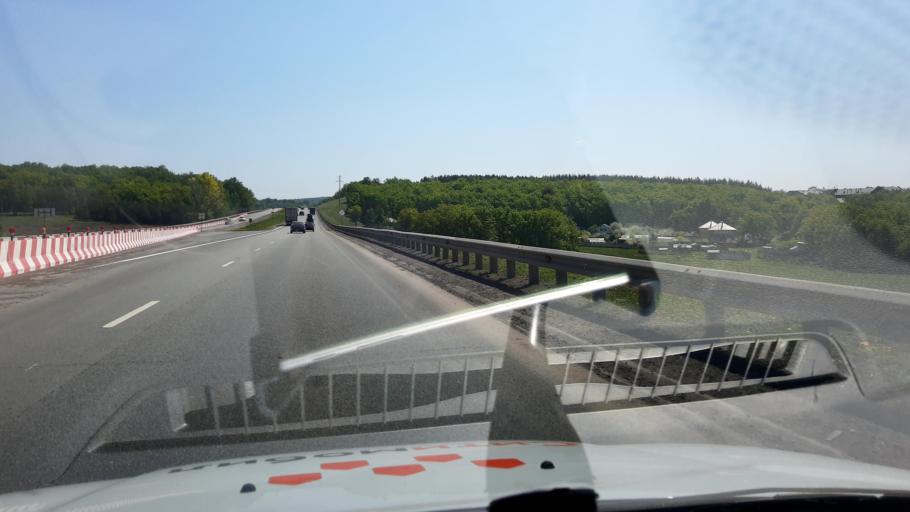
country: RU
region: Bashkortostan
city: Avdon
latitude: 54.6418
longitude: 55.5770
